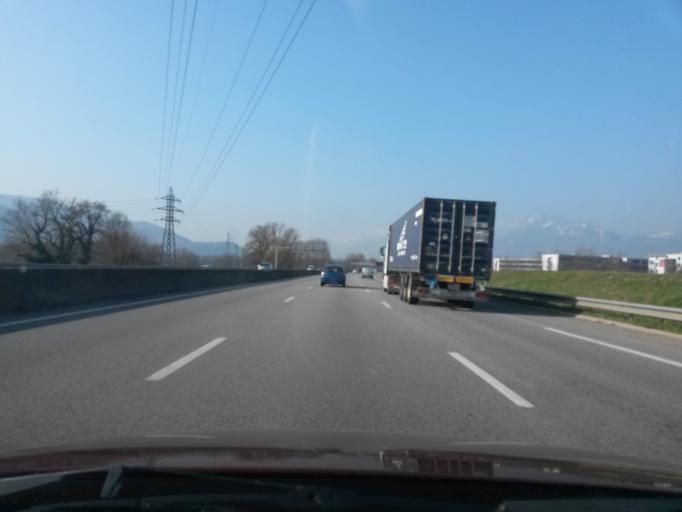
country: FR
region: Rhone-Alpes
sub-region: Departement de l'Isere
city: Montbonnot-Saint-Martin
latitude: 45.2150
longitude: 5.8138
